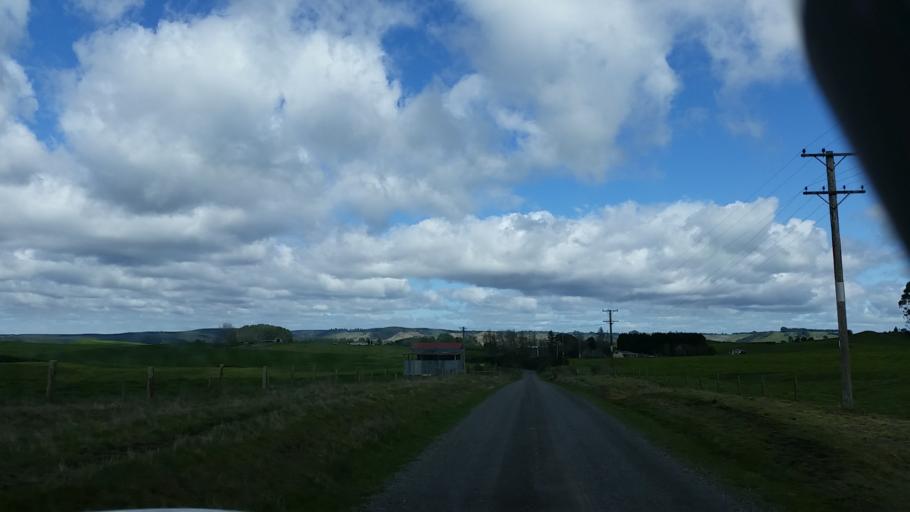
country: NZ
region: Bay of Plenty
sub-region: Whakatane District
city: Murupara
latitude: -38.3029
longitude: 176.5623
